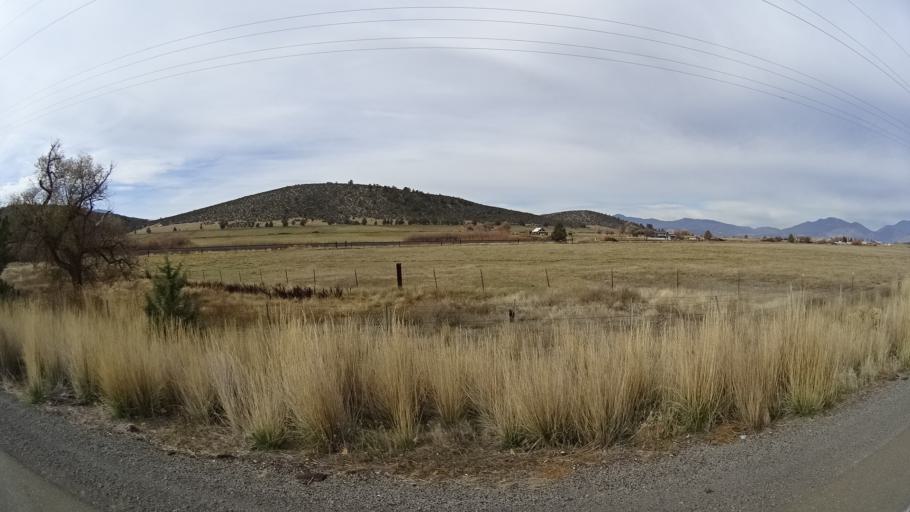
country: US
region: California
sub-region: Siskiyou County
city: Montague
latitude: 41.6904
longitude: -122.5350
